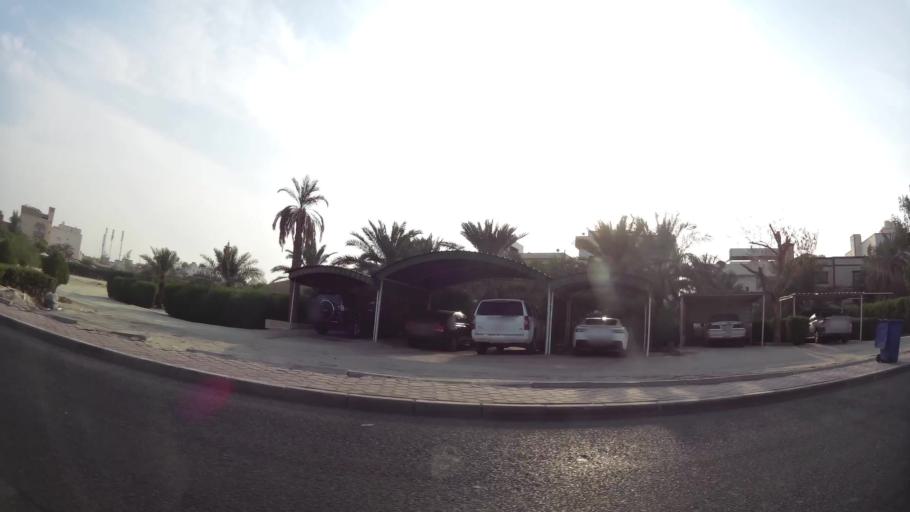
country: KW
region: Mubarak al Kabir
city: Mubarak al Kabir
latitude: 29.1836
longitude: 48.0734
